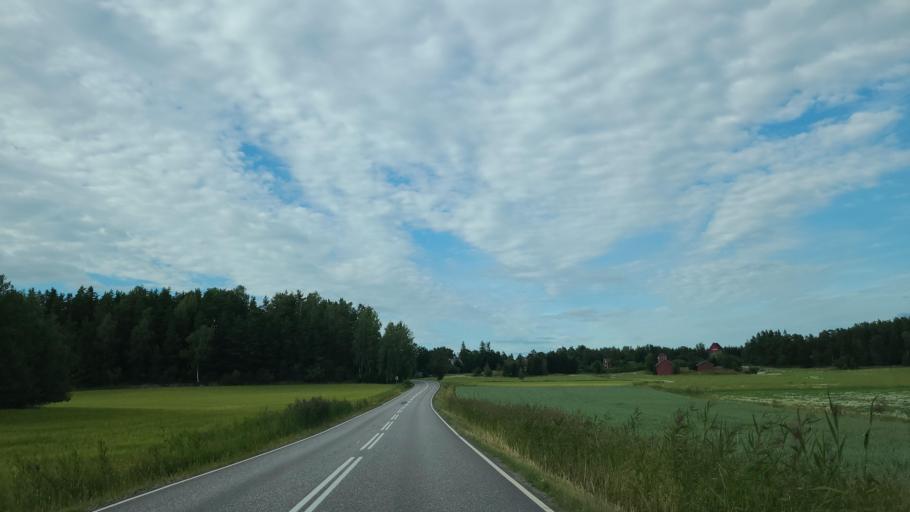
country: FI
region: Varsinais-Suomi
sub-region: Turku
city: Rymaettylae
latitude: 60.3499
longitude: 21.9574
